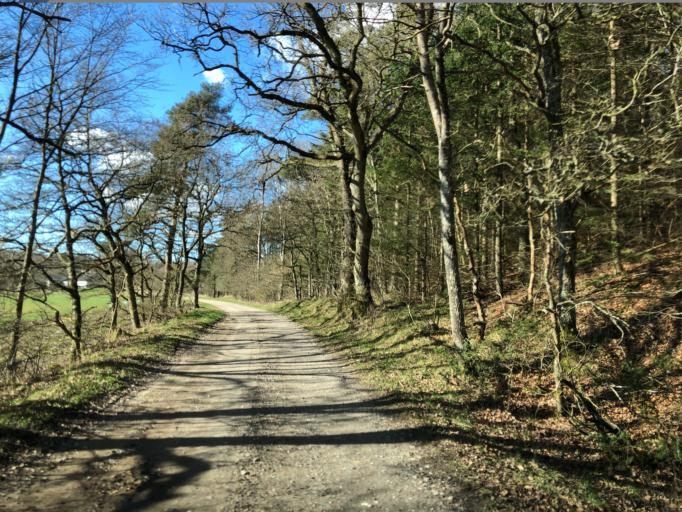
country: DK
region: Central Jutland
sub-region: Favrskov Kommune
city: Hammel
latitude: 56.3136
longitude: 9.9099
